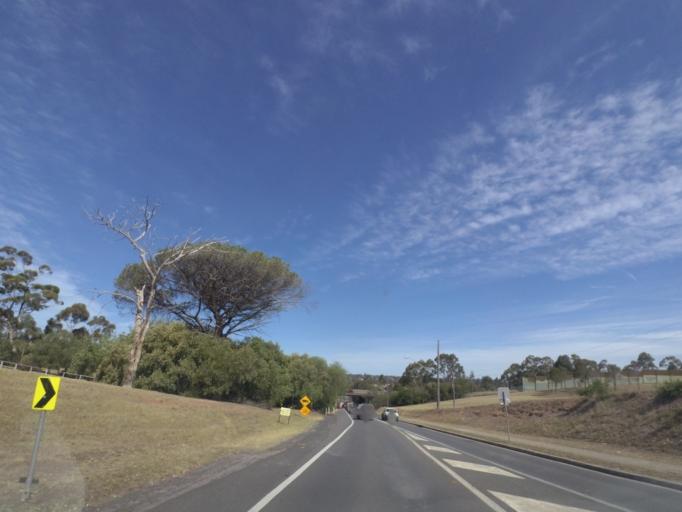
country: AU
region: New South Wales
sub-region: Campbelltown Municipality
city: Campbelltown
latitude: -34.0518
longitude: 150.8068
